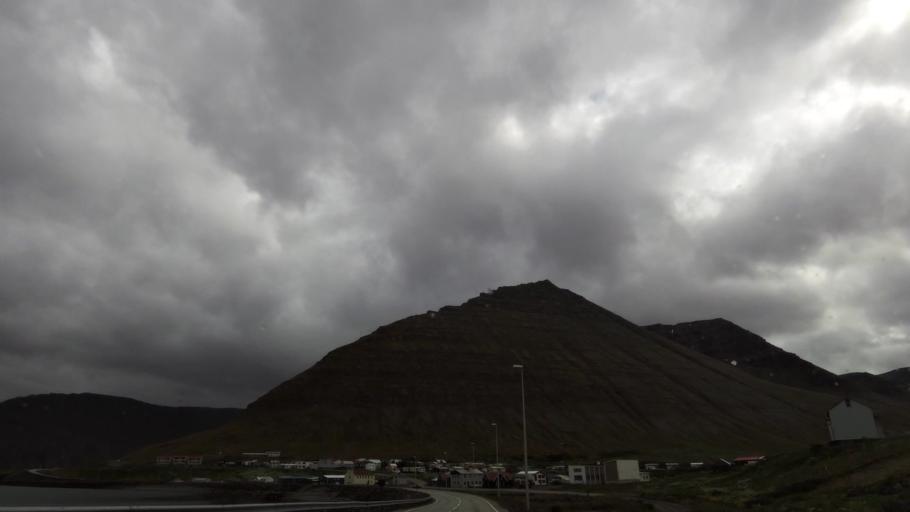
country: IS
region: Westfjords
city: Isafjoerdur
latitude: 66.1140
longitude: -23.1211
